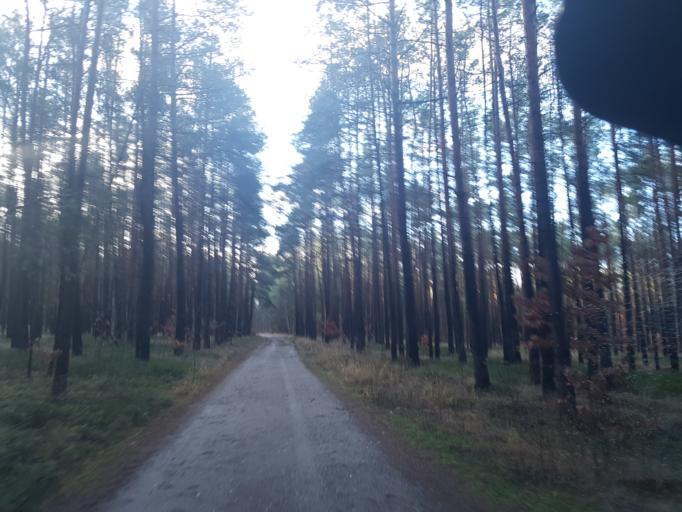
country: DE
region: Brandenburg
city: Ruckersdorf
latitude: 51.5850
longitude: 13.6014
